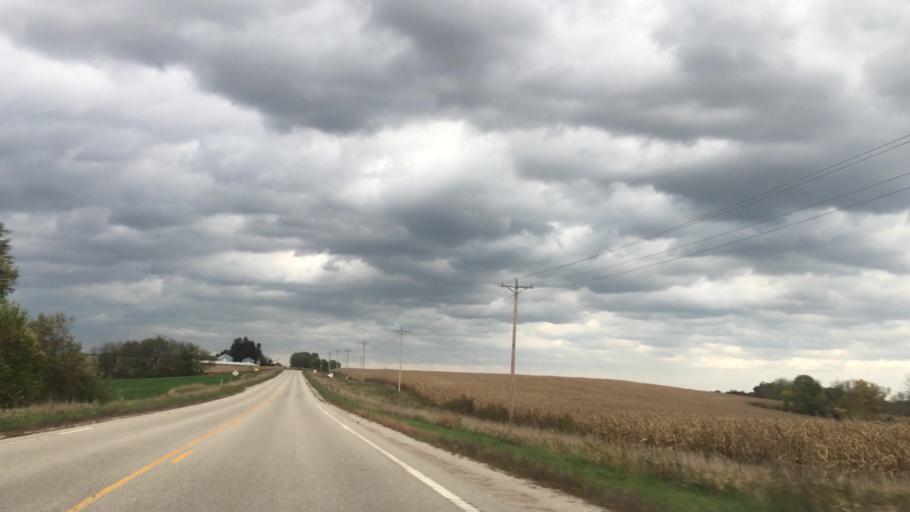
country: US
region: Minnesota
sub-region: Fillmore County
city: Preston
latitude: 43.7321
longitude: -92.0332
